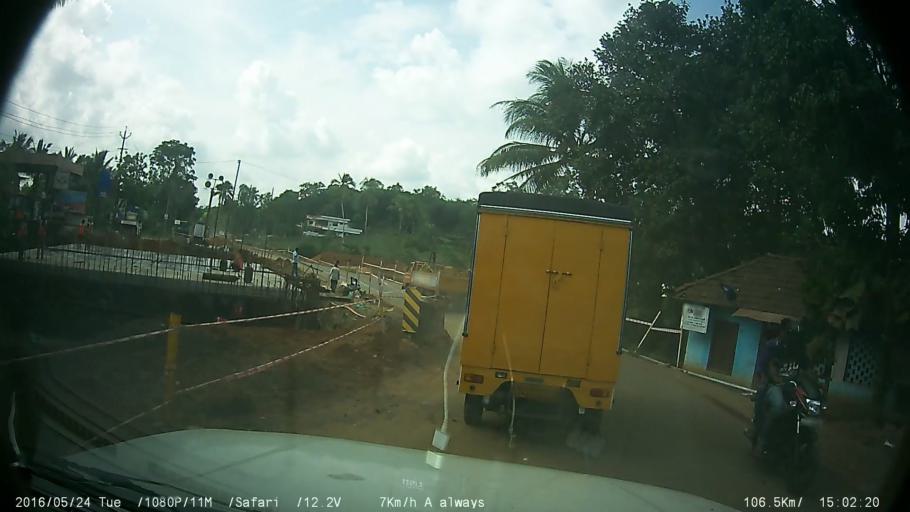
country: IN
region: Kerala
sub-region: Ernakulam
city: Piravam
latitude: 9.8415
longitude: 76.5922
